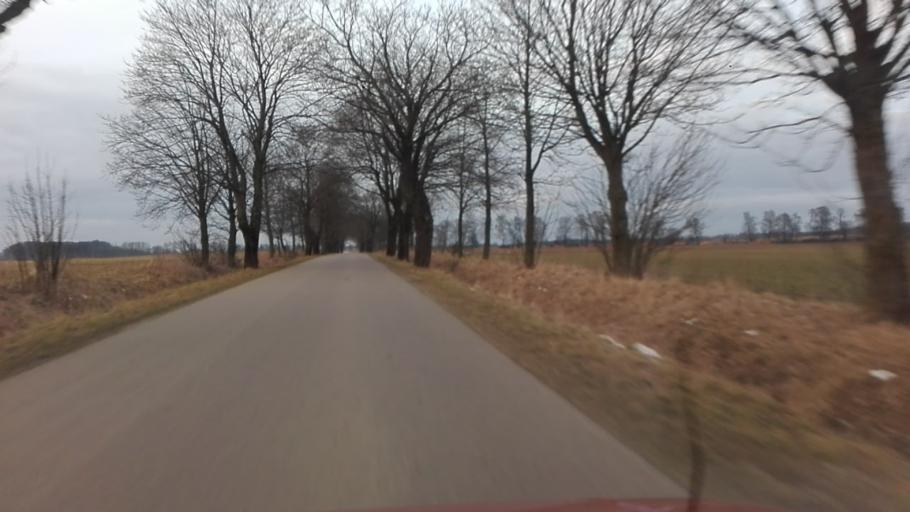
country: PL
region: West Pomeranian Voivodeship
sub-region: Powiat swidwinski
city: Rabino
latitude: 53.8114
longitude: 15.9199
